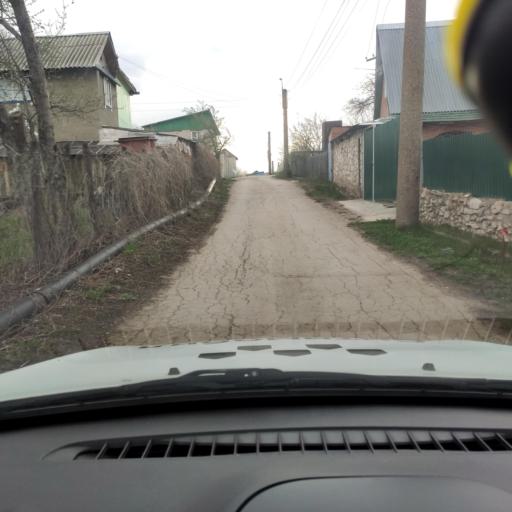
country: RU
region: Samara
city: Mezhdurechensk
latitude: 53.2444
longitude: 49.1524
